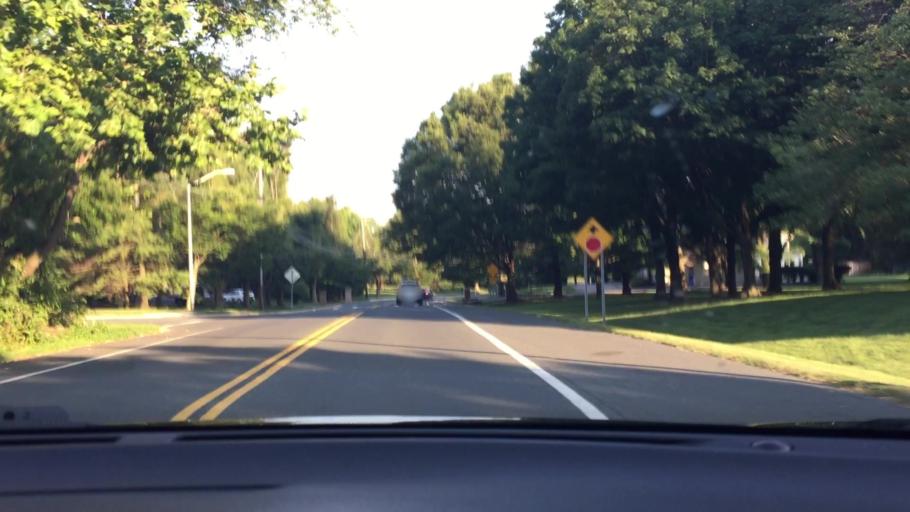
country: US
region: Maryland
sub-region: Montgomery County
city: Potomac
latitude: 39.0219
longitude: -77.1822
